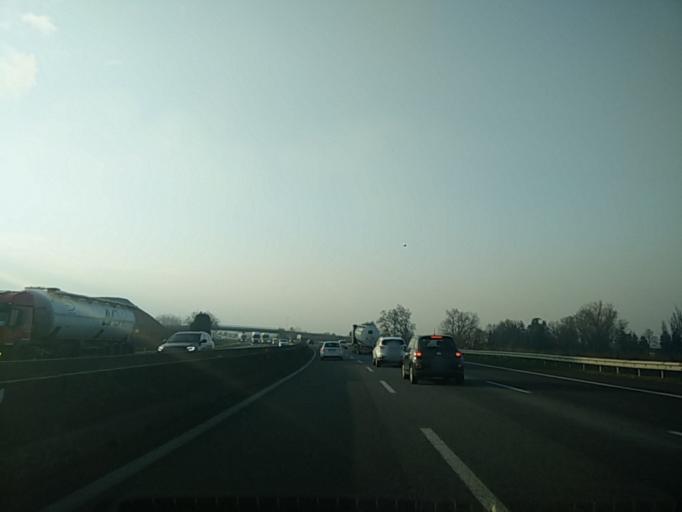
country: IT
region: Emilia-Romagna
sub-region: Provincia di Ravenna
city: Solarolo
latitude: 44.3373
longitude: 11.8712
